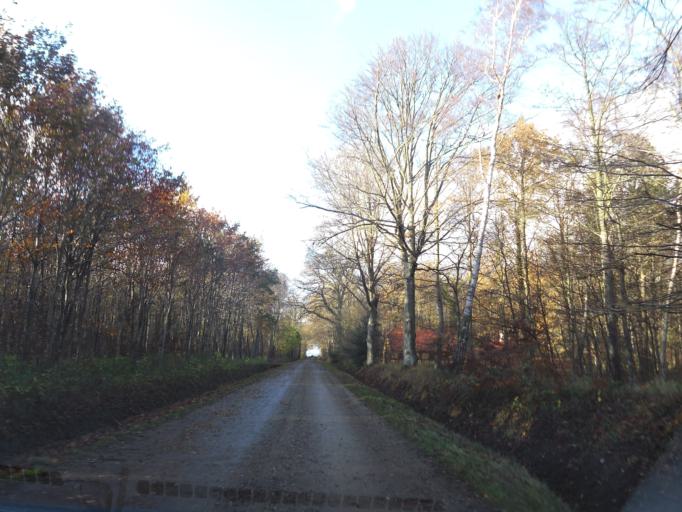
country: DK
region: Central Jutland
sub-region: Odder Kommune
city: Odder
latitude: 55.8551
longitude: 10.1643
